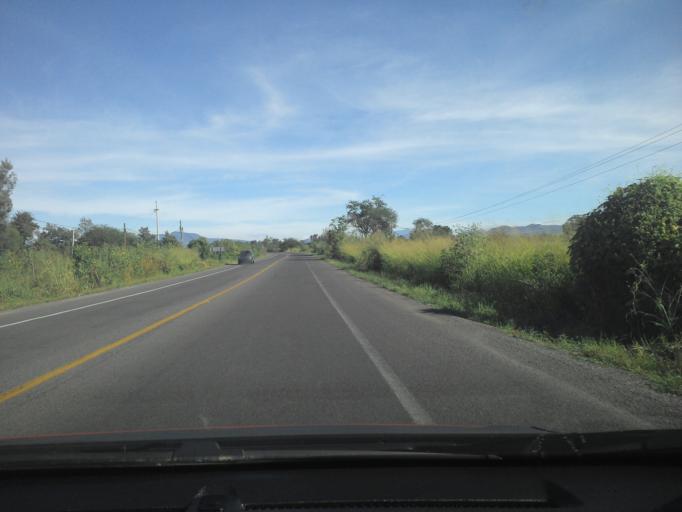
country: MX
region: Jalisco
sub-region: Teuchitlan
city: La Estanzuela
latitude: 20.6759
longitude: -103.8336
